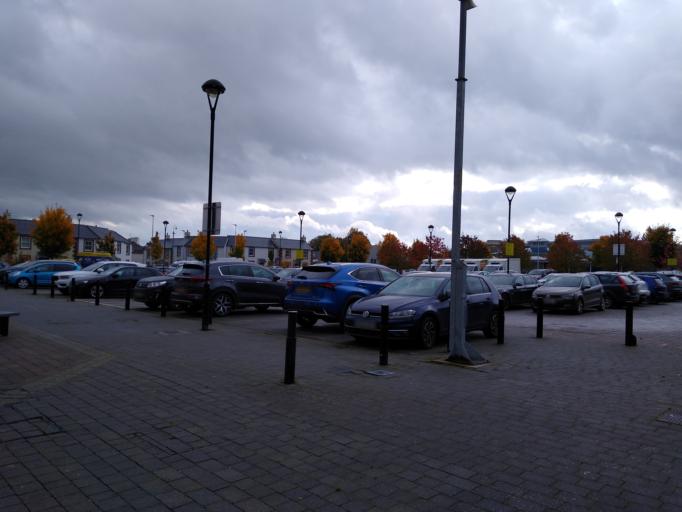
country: GB
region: England
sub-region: Cumbria
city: Penrith
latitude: 54.6615
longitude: -2.7512
